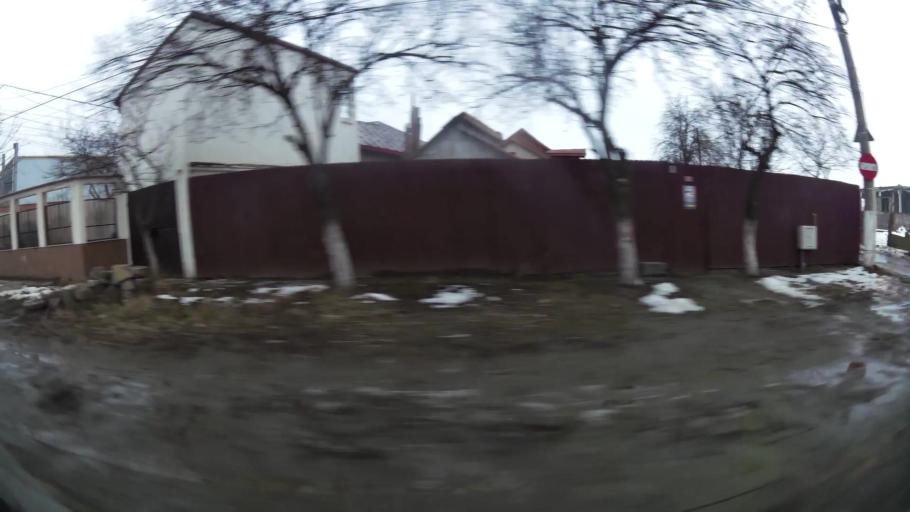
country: RO
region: Ilfov
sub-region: Comuna Magurele
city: Magurele
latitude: 44.3778
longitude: 26.0472
